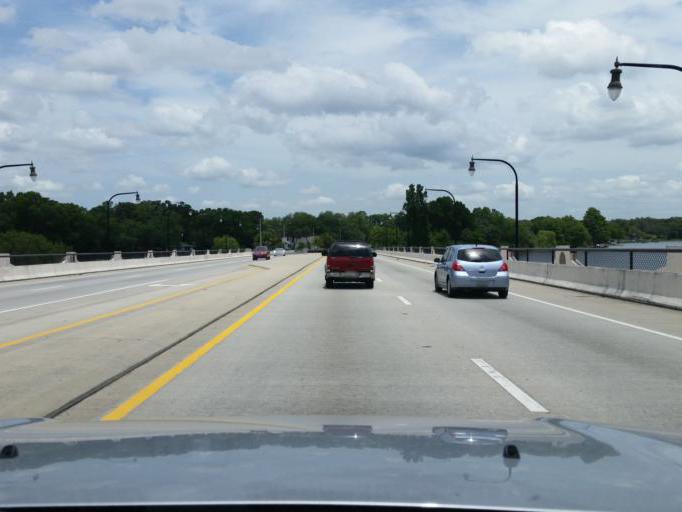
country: US
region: Florida
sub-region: Hillsborough County
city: Temple Terrace
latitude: 28.0087
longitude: -82.4144
